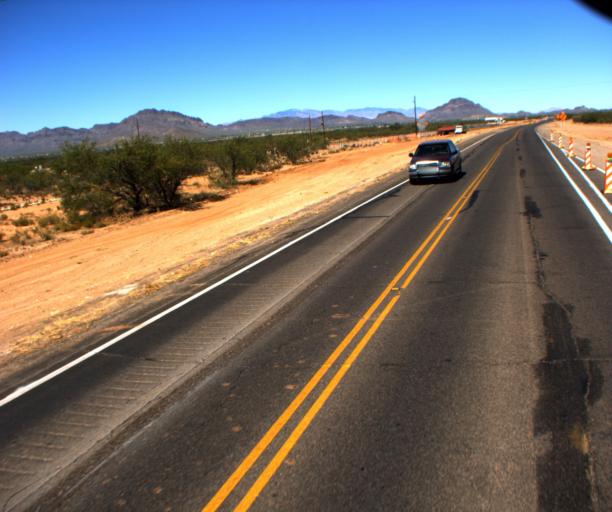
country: US
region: Arizona
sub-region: Pima County
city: Valencia West
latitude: 32.1368
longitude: -111.1625
